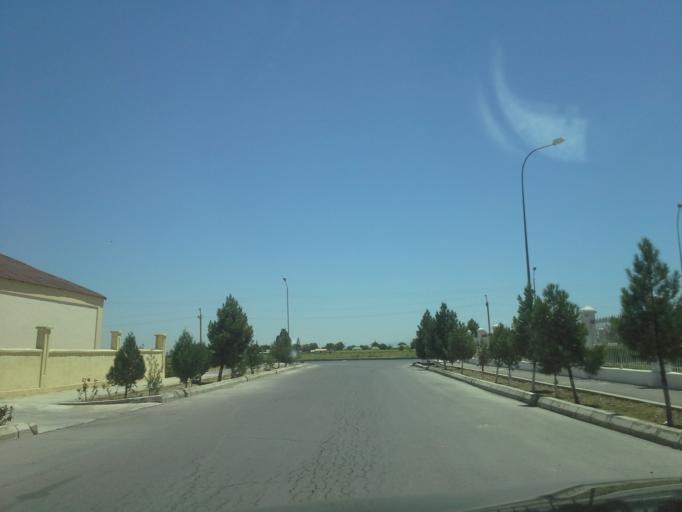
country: TM
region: Ahal
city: Abadan
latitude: 38.0358
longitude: 58.2701
